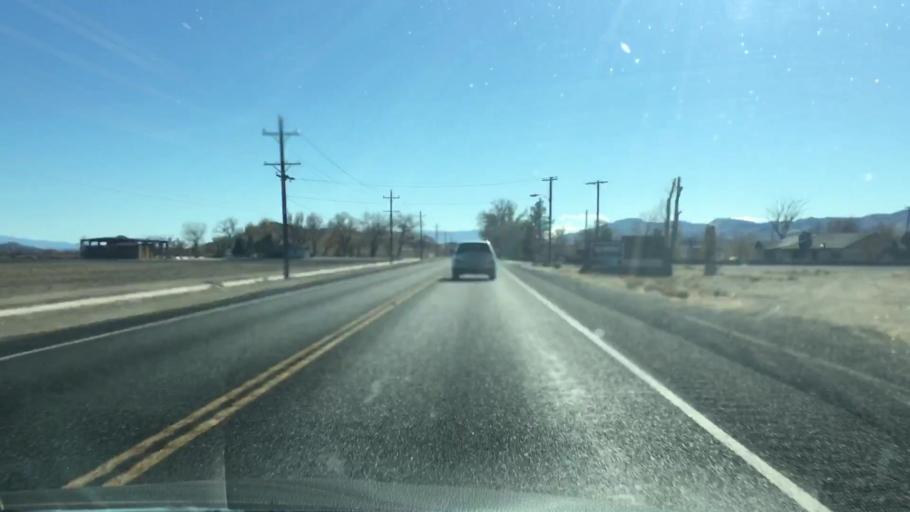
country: US
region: Nevada
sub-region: Lyon County
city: Yerington
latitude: 39.0350
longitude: -119.1816
